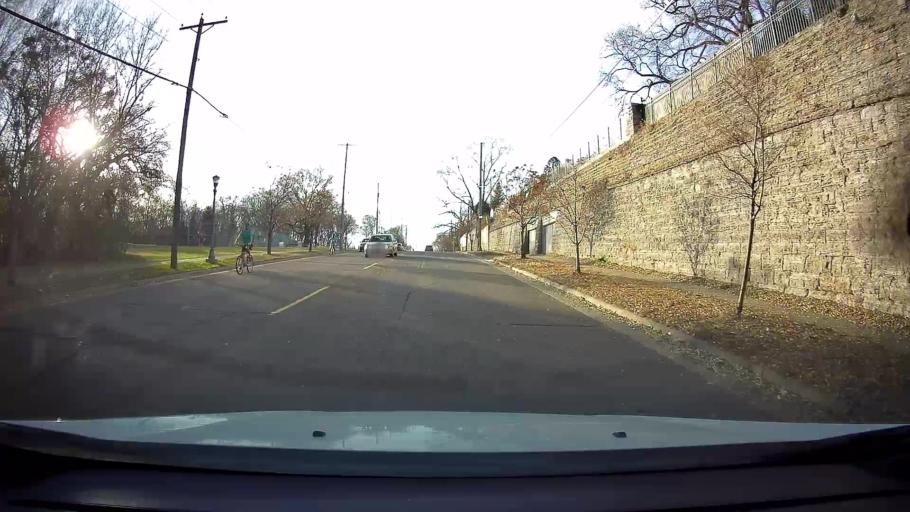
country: US
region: Minnesota
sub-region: Dakota County
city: West Saint Paul
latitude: 44.9341
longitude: -93.1313
